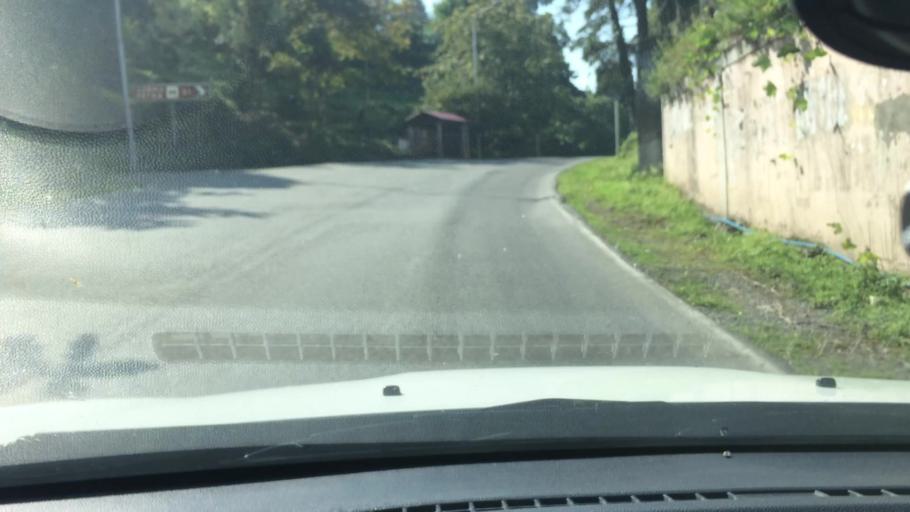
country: GE
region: Ajaria
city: Kobuleti
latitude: 41.7678
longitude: 41.7545
